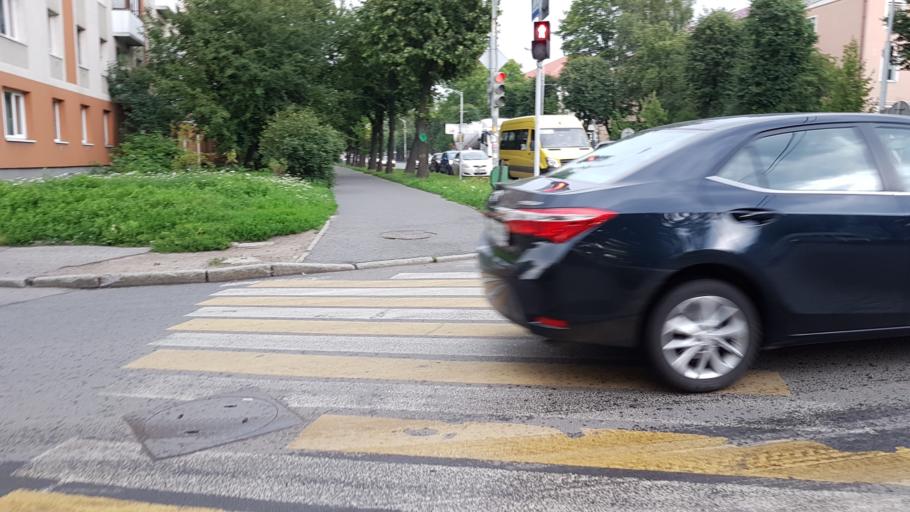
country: RU
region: Kaliningrad
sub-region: Gorod Kaliningrad
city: Kaliningrad
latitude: 54.7281
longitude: 20.5283
